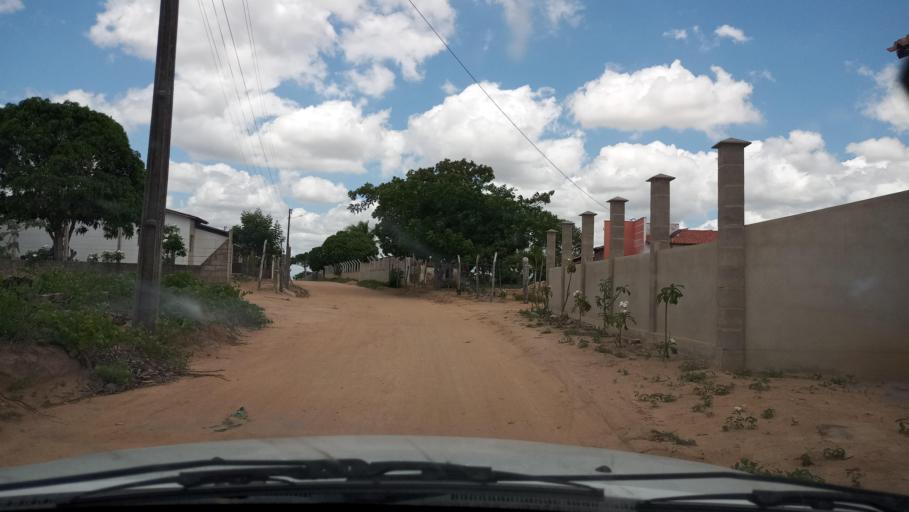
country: BR
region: Rio Grande do Norte
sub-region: Sao Jose Do Campestre
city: Sao Jose do Campestre
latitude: -6.4352
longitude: -35.6343
